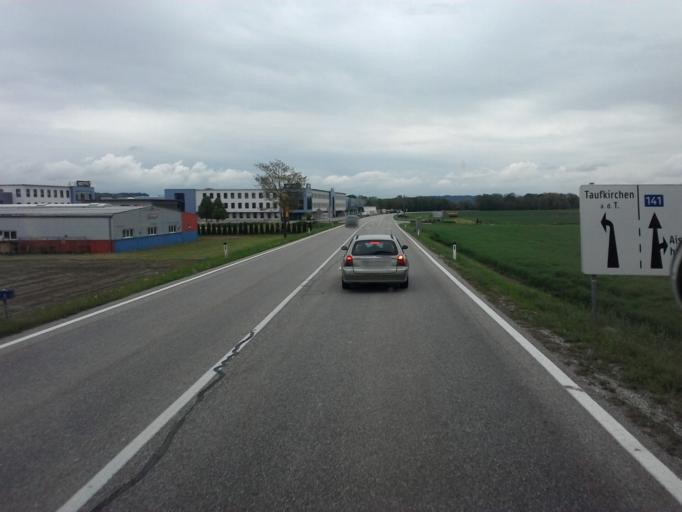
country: AT
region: Upper Austria
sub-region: Politischer Bezirk Grieskirchen
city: Grieskirchen
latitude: 48.2244
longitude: 13.7374
